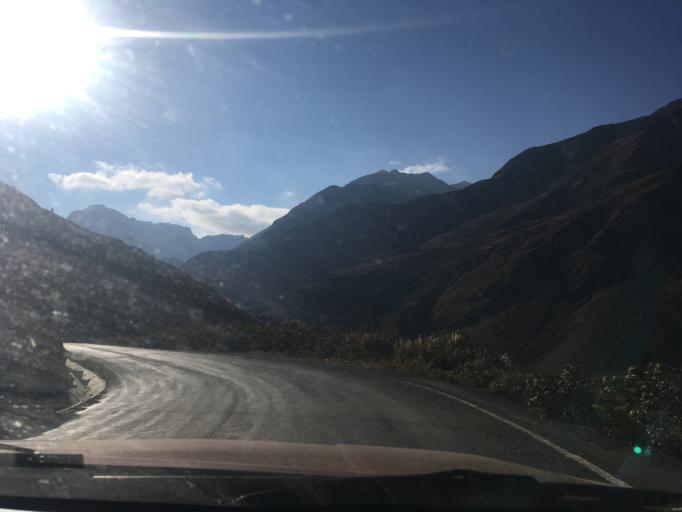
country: BO
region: La Paz
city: Quime
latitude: -17.0022
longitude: -67.2723
